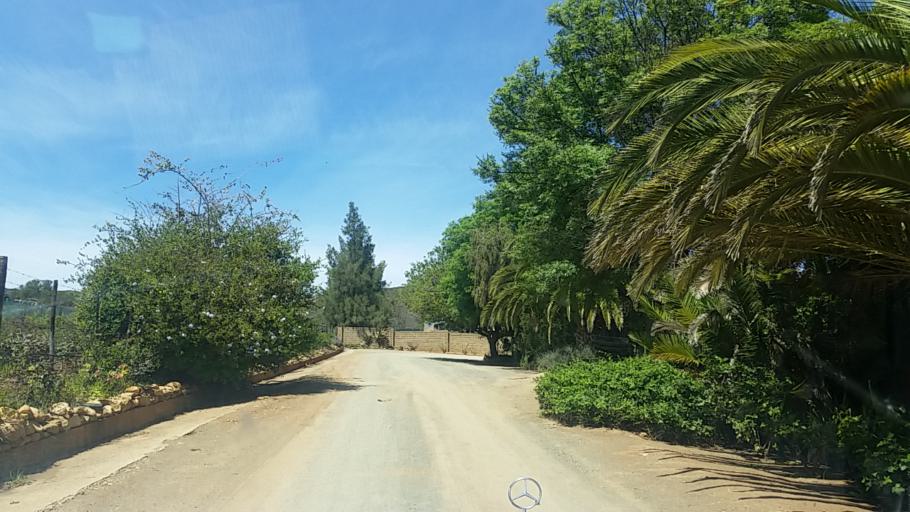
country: ZA
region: Western Cape
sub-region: Eden District Municipality
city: Knysna
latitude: -33.6500
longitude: 23.1356
